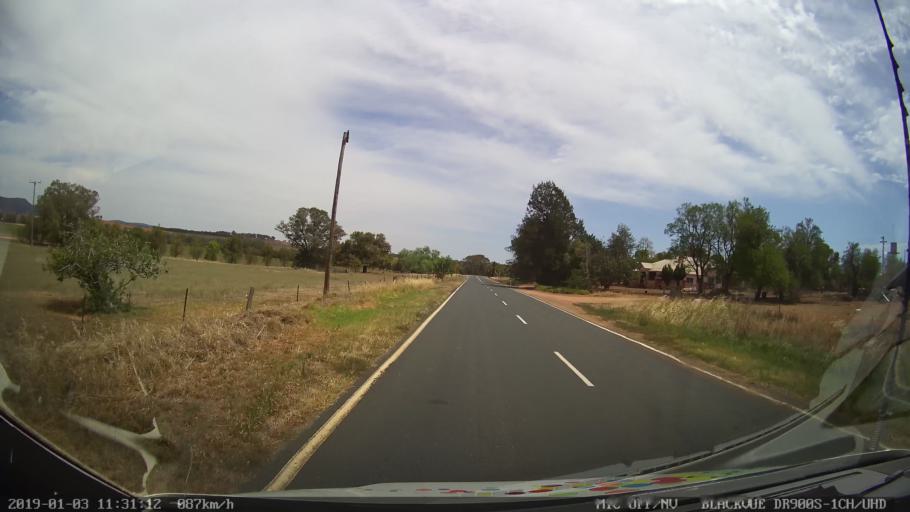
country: AU
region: New South Wales
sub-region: Weddin
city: Grenfell
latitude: -33.9732
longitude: 148.1854
